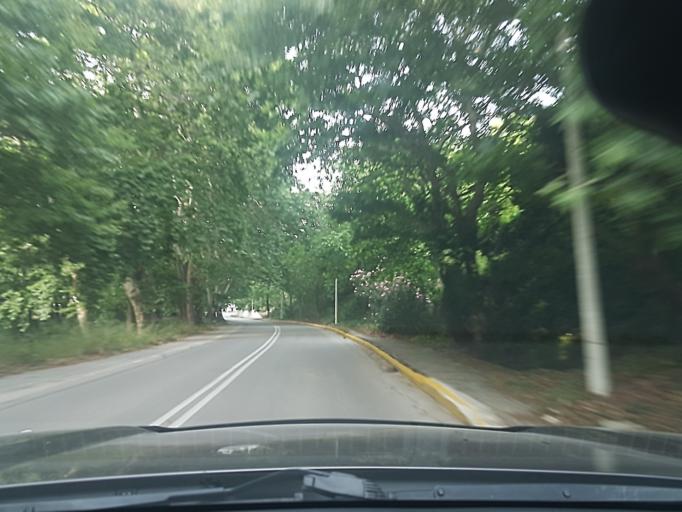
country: GR
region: Central Greece
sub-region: Nomos Evvoias
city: Yimnon
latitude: 38.5785
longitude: 23.8342
